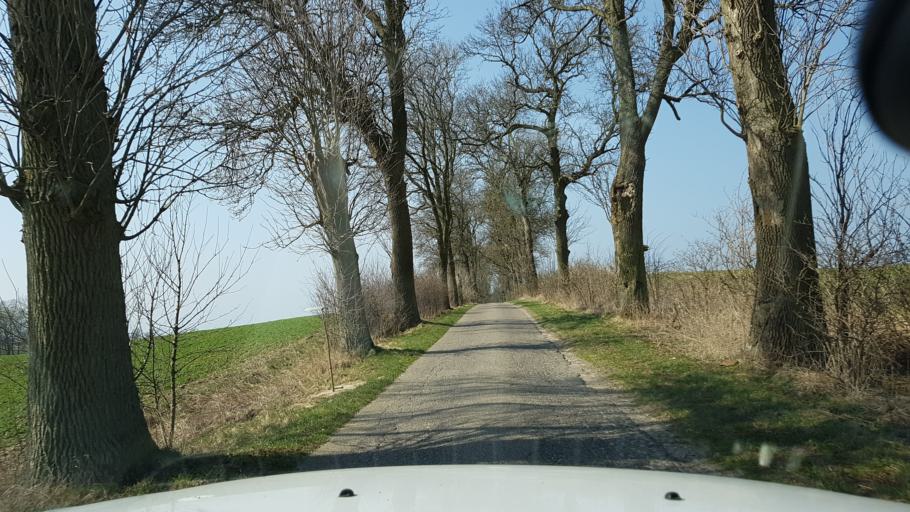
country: PL
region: West Pomeranian Voivodeship
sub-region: Powiat slawienski
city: Darlowo
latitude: 54.4689
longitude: 16.4869
